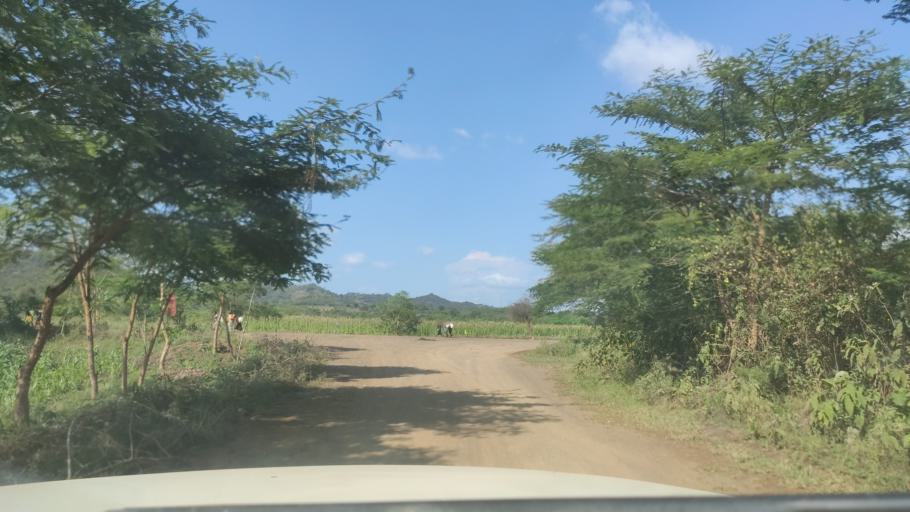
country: ET
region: Southern Nations, Nationalities, and People's Region
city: Felege Neway
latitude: 6.3939
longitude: 37.1007
